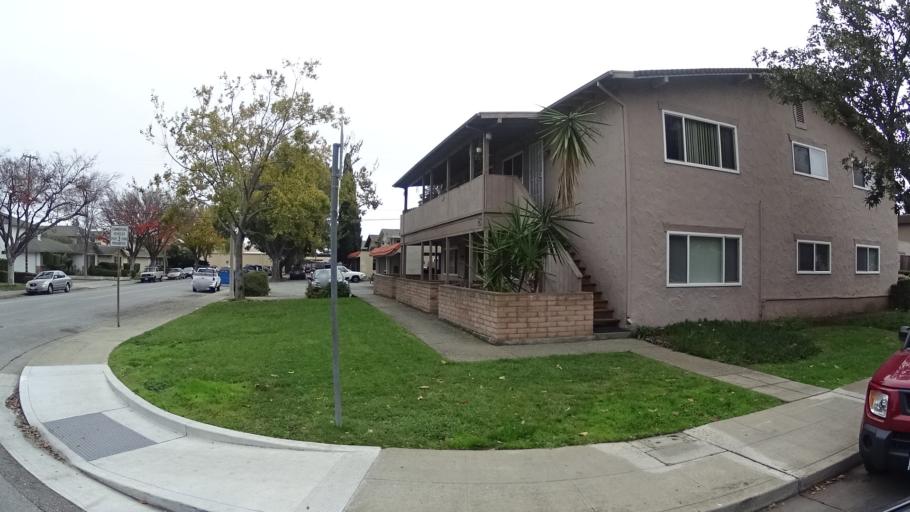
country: US
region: California
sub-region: Santa Clara County
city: Sunnyvale
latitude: 37.3655
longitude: -122.0172
